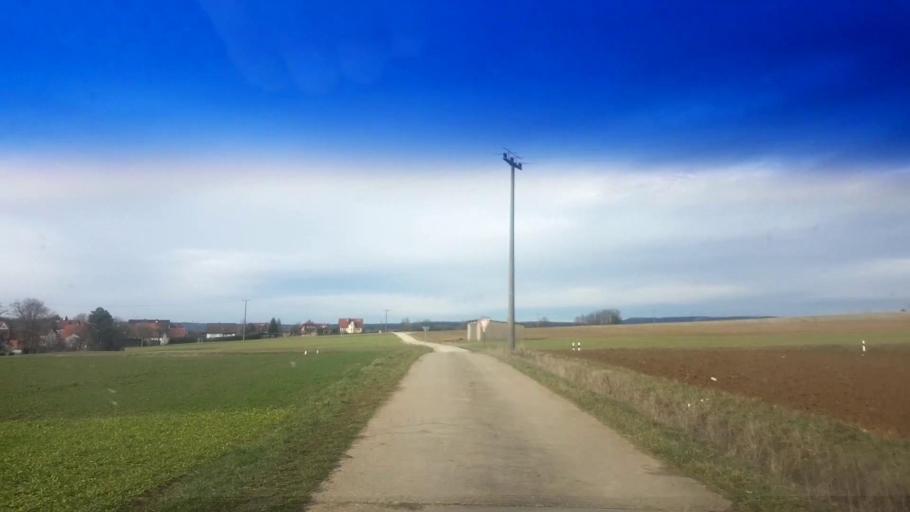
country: DE
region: Bavaria
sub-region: Upper Franconia
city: Litzendorf
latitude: 49.9373
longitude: 10.9961
